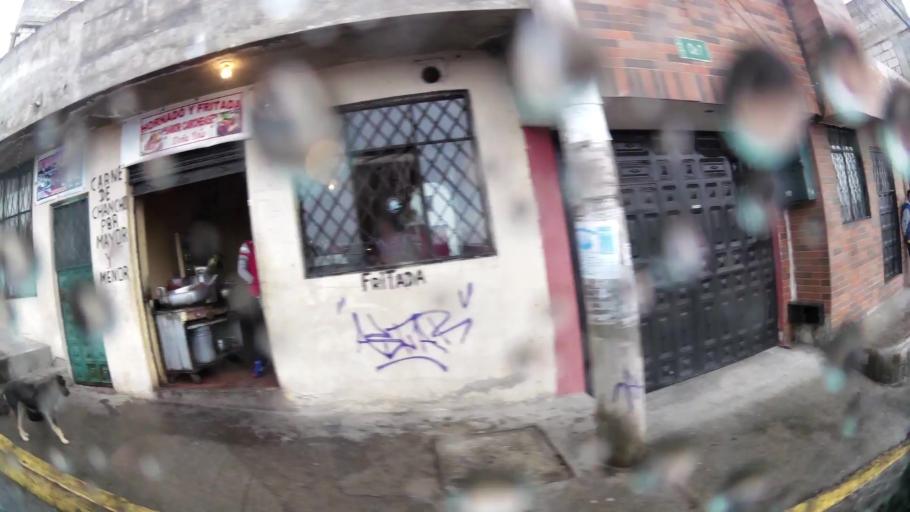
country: EC
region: Pichincha
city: Quito
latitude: -0.0954
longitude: -78.5077
